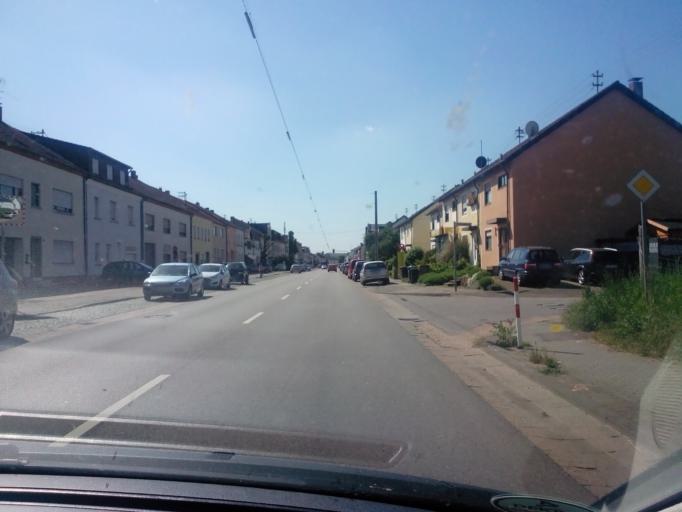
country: DE
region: Saarland
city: Saarlouis
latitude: 49.3043
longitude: 6.7579
